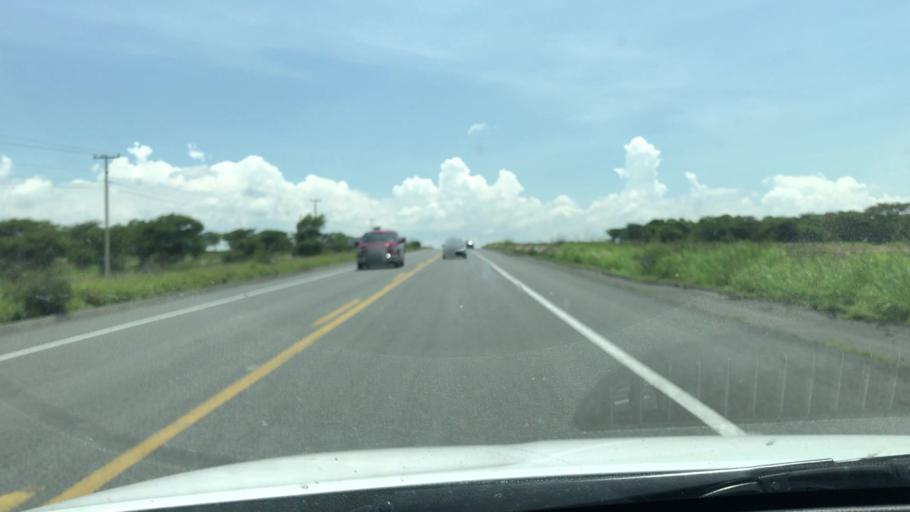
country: MX
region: Jalisco
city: Degollado
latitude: 20.3567
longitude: -102.1518
